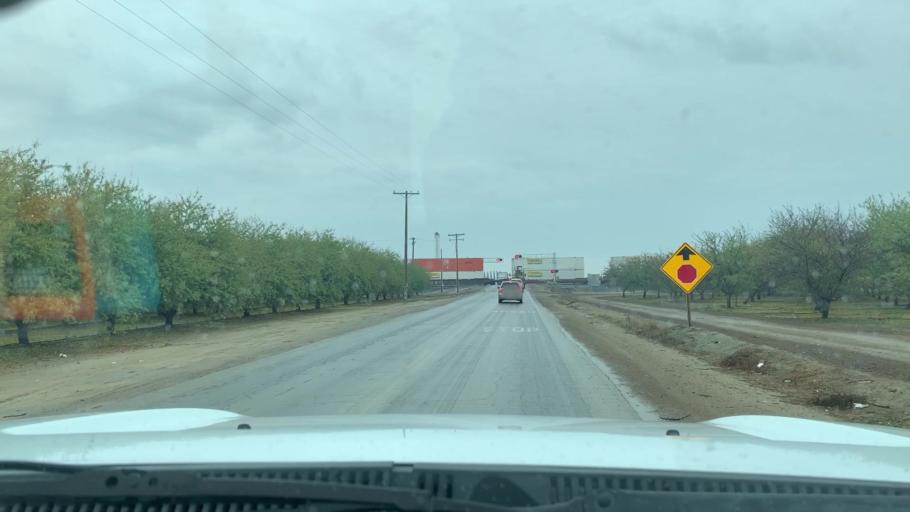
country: US
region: California
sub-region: Kern County
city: Delano
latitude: 35.7612
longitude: -119.3473
